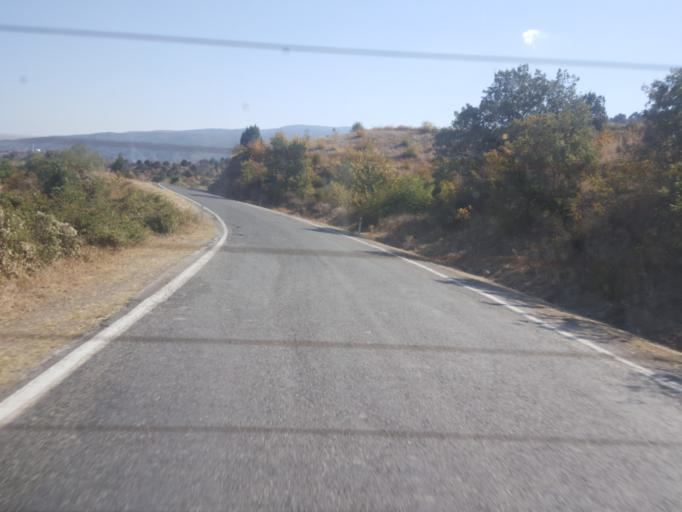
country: TR
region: Kastamonu
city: Tosya
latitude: 40.9943
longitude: 34.1313
